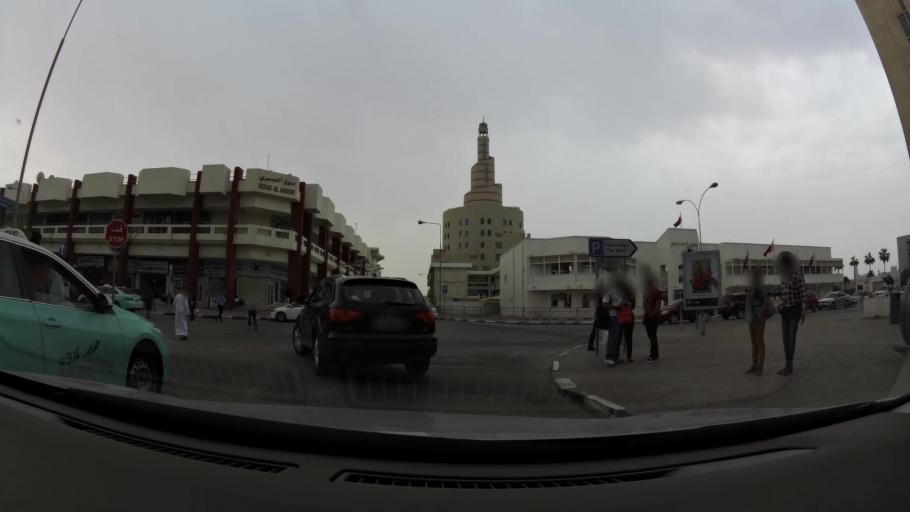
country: QA
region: Baladiyat ad Dawhah
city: Doha
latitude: 25.2885
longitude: 51.5375
